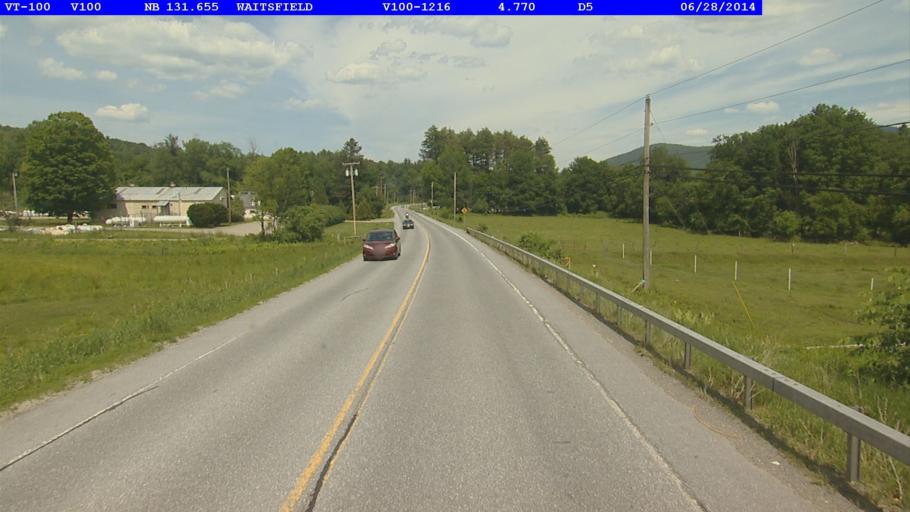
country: US
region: Vermont
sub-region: Washington County
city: Waterbury
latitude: 44.2029
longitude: -72.8105
